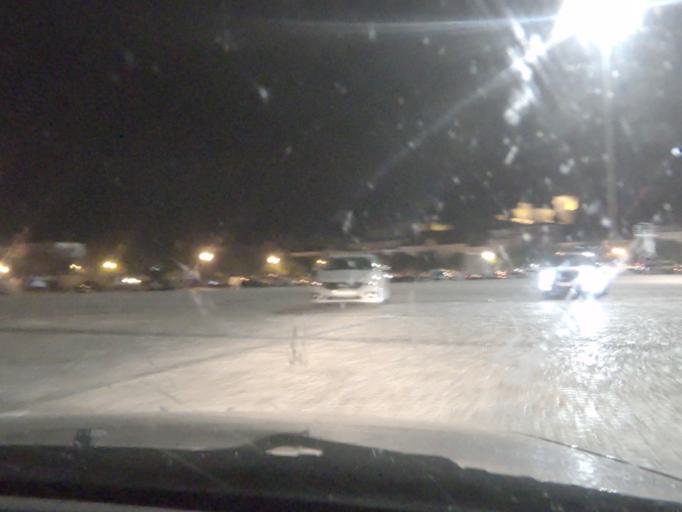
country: PT
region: Evora
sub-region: Estremoz
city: Estremoz
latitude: 38.8429
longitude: -7.5855
